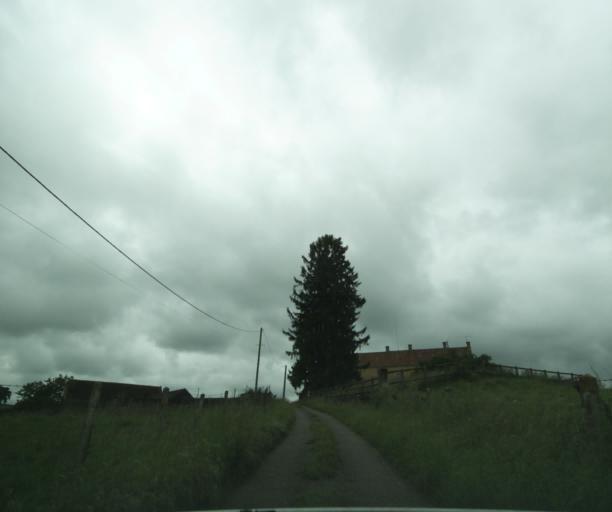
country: FR
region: Bourgogne
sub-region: Departement de Saone-et-Loire
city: Charolles
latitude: 46.4742
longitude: 4.3176
